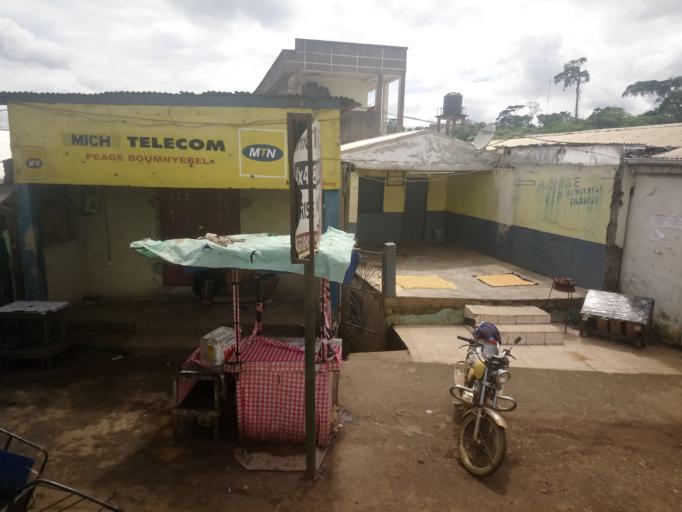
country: CM
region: Centre
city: Eseka
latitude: 3.8833
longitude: 10.8501
